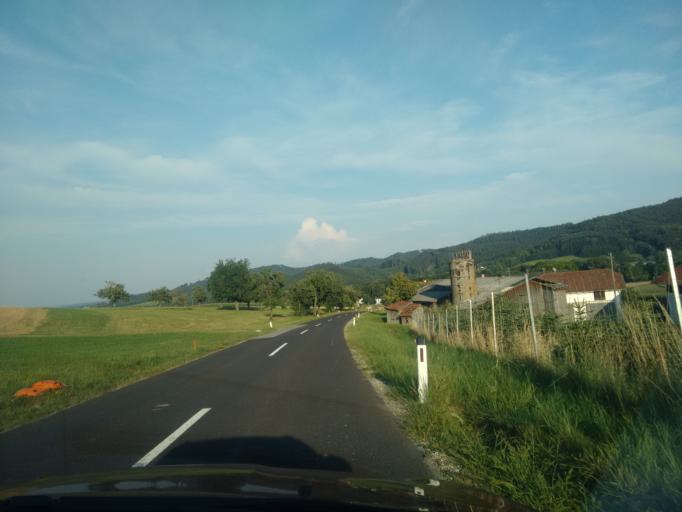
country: AT
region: Upper Austria
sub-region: Politischer Bezirk Vocklabruck
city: Wolfsegg am Hausruck
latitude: 48.1491
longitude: 13.6221
